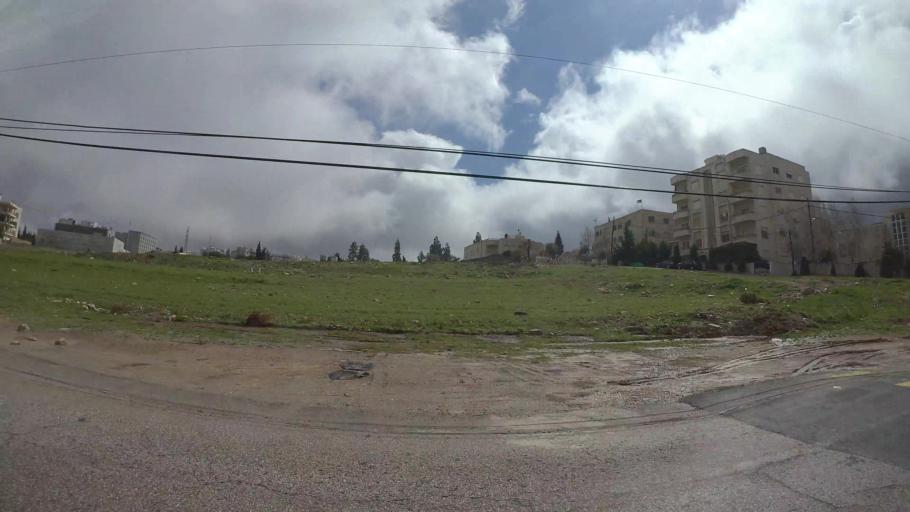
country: JO
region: Amman
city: Wadi as Sir
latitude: 31.9419
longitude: 35.8541
